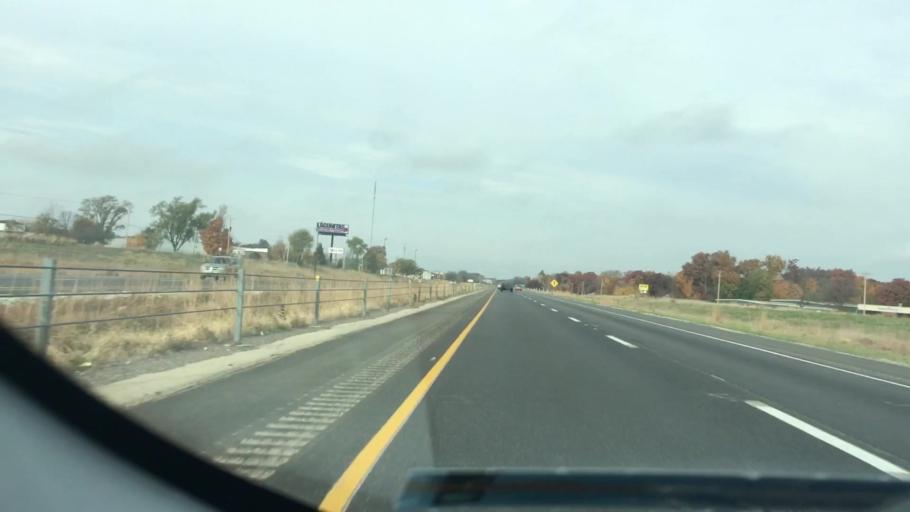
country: US
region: Illinois
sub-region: Tazewell County
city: East Peoria
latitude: 40.6431
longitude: -89.5412
